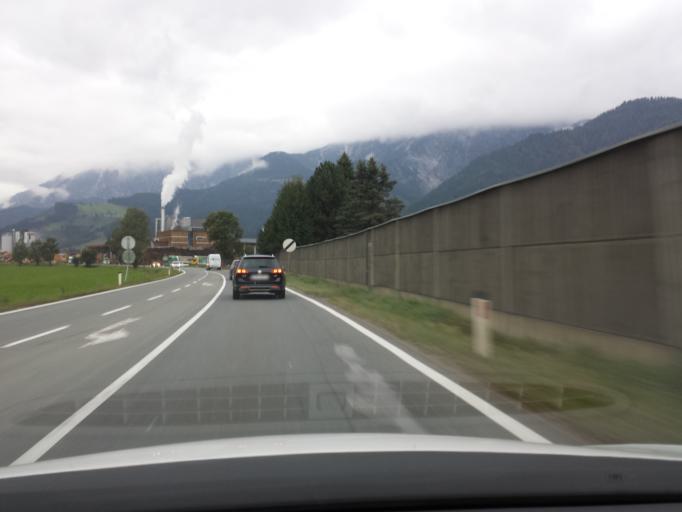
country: AT
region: Salzburg
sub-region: Politischer Bezirk Zell am See
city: Saalfelden am Steinernen Meer
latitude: 47.4393
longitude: 12.8192
